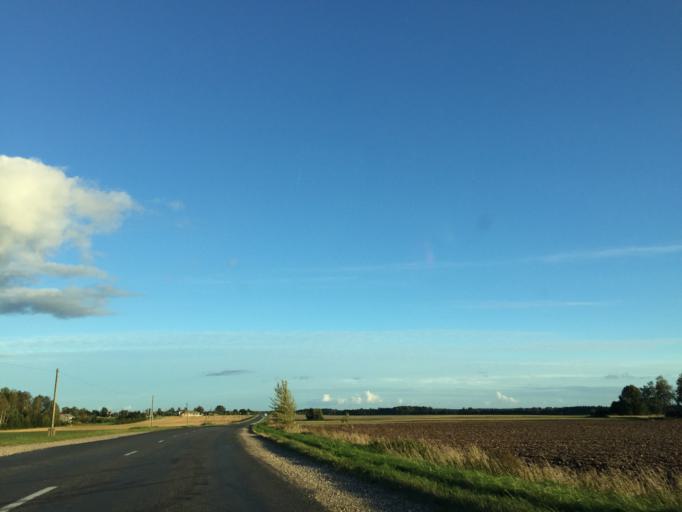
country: LV
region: Saldus Rajons
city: Saldus
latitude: 56.7040
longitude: 22.4275
